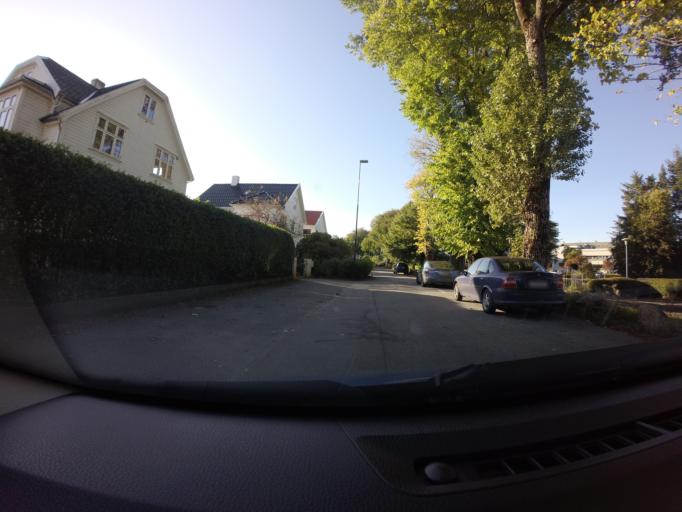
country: NO
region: Rogaland
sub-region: Stavanger
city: Stavanger
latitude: 58.9509
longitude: 5.7340
